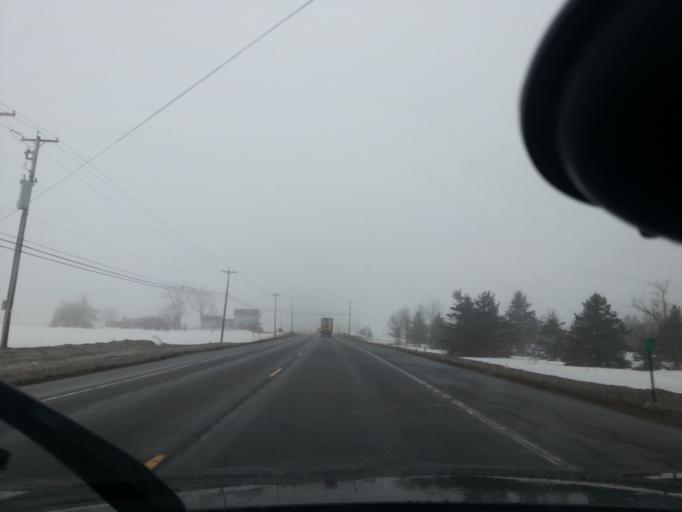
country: US
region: New York
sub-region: Jefferson County
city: Philadelphia
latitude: 44.1350
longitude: -75.7303
